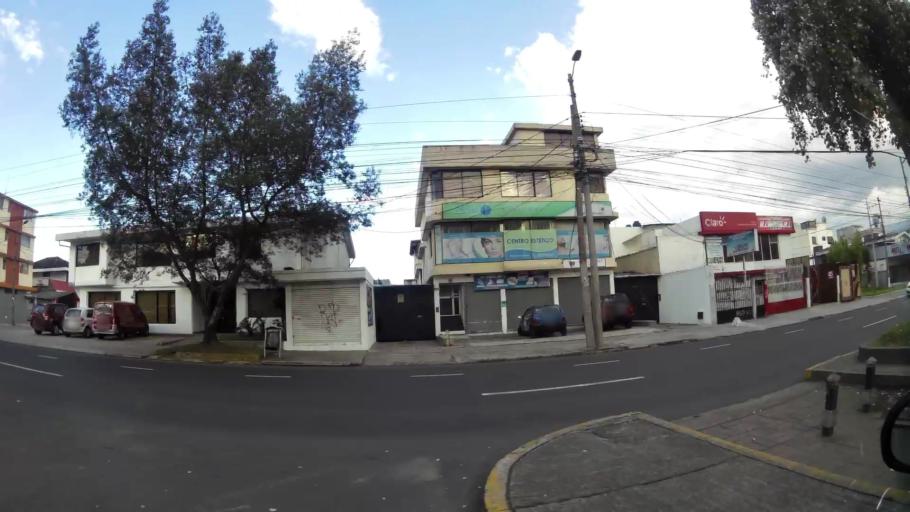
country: EC
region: Pichincha
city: Quito
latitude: -0.1609
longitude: -78.4829
